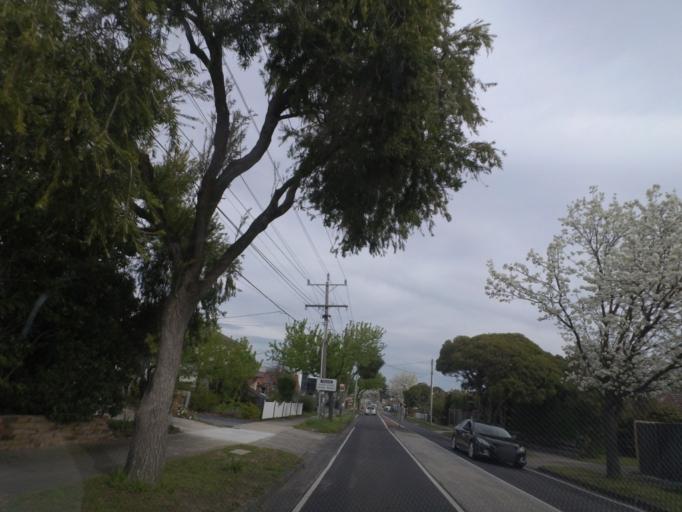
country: AU
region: Victoria
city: Forest Hill
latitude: -37.8288
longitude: 145.1868
